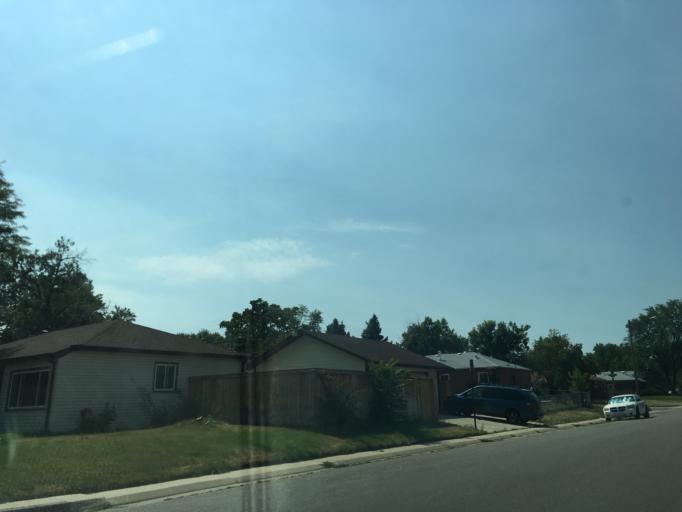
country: US
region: Colorado
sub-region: Jefferson County
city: Lakewood
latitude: 39.6923
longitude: -105.0485
